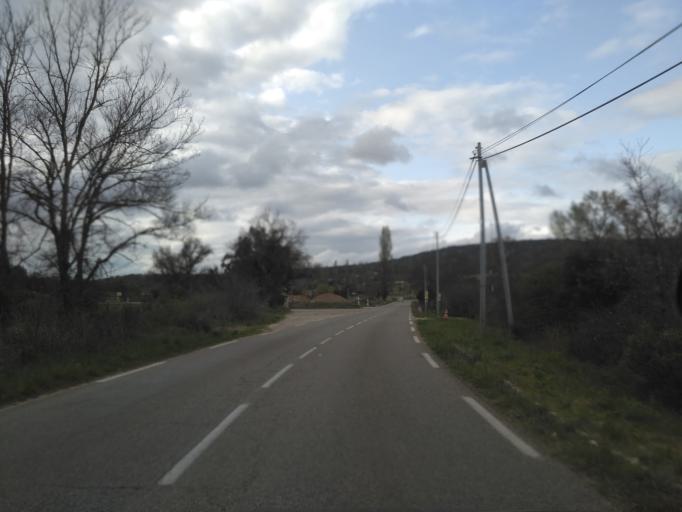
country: FR
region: Provence-Alpes-Cote d'Azur
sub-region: Departement du Var
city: Barjols
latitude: 43.5784
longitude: 6.0155
